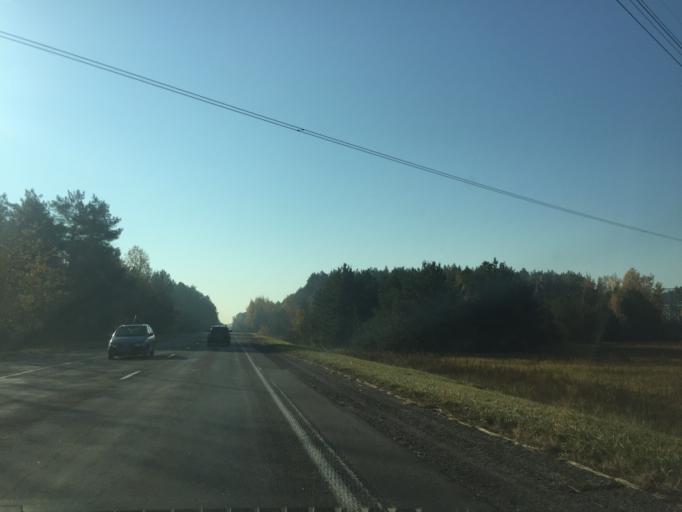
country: BY
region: Gomel
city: Kastsyukowka
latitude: 52.4359
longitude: 30.8264
